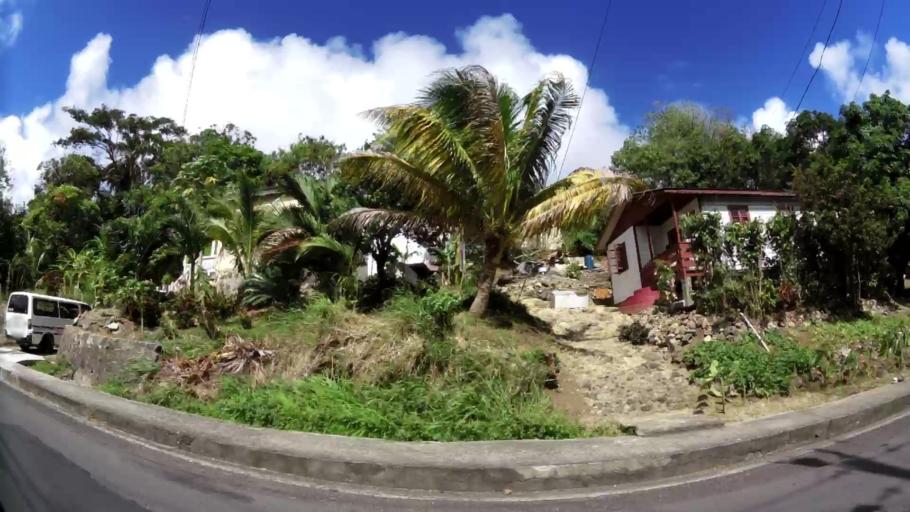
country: LC
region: Dennery Quarter
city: Dennery
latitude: 13.9329
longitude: -60.9082
